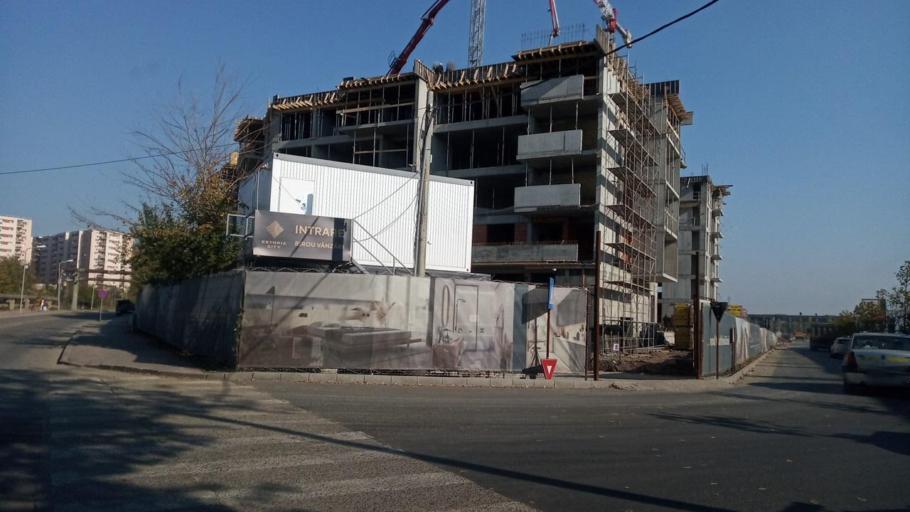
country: RO
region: Ilfov
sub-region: Comuna Glina
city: Catelu
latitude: 44.4100
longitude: 26.1951
